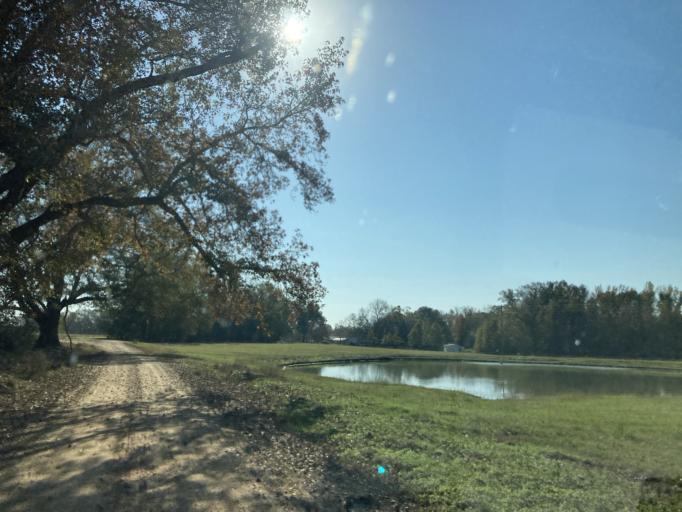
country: US
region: Mississippi
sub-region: Madison County
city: Kearney Park
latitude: 32.7263
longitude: -90.3091
